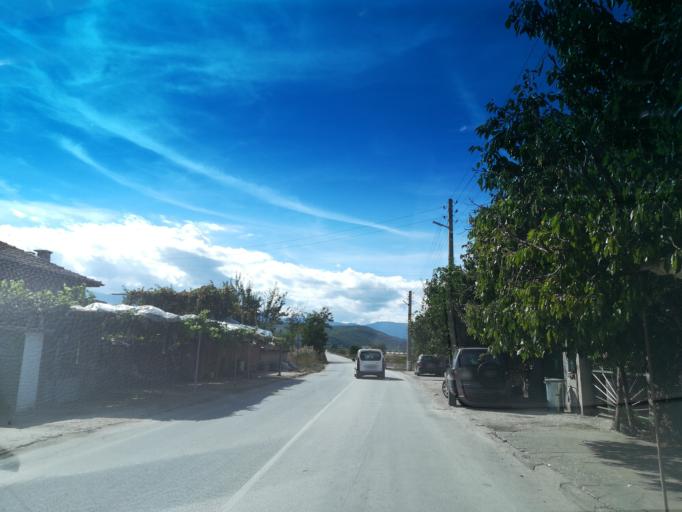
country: BG
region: Plovdiv
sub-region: Obshtina Krichim
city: Krichim
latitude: 42.0826
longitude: 24.4233
